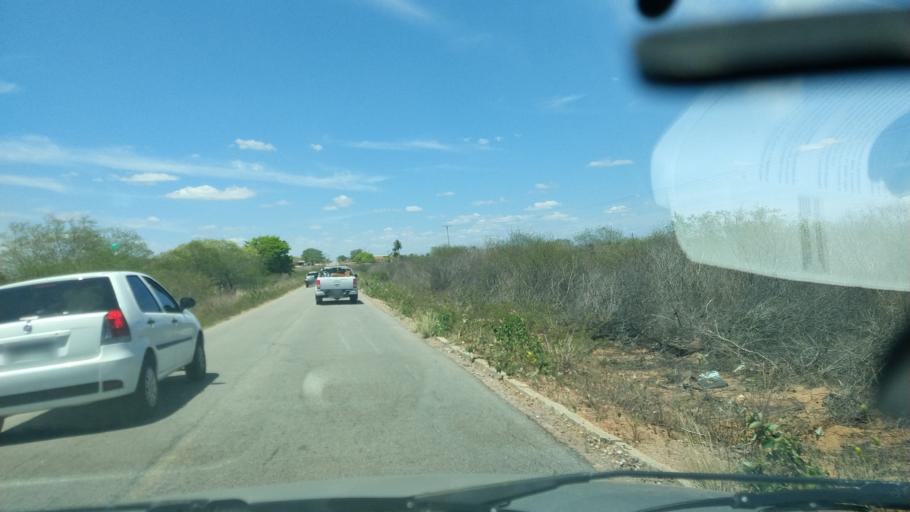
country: BR
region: Rio Grande do Norte
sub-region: Sao Paulo Do Potengi
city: Sao Paulo do Potengi
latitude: -5.9210
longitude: -35.5812
